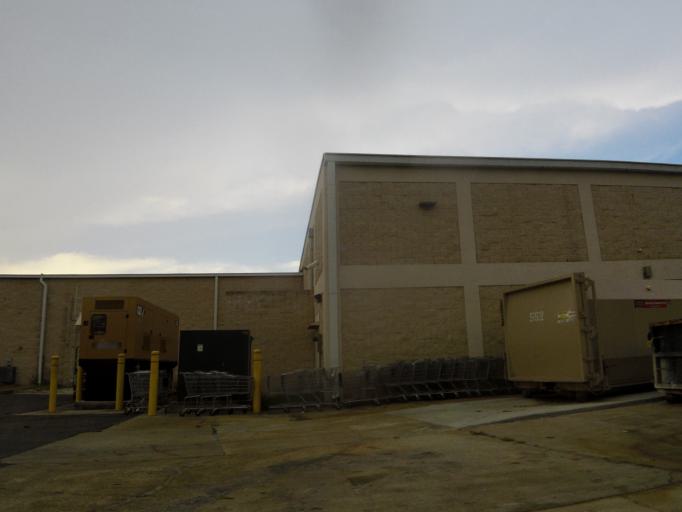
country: US
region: Florida
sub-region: Saint Johns County
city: Ponte Vedra Beach
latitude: 30.2532
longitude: -81.3926
